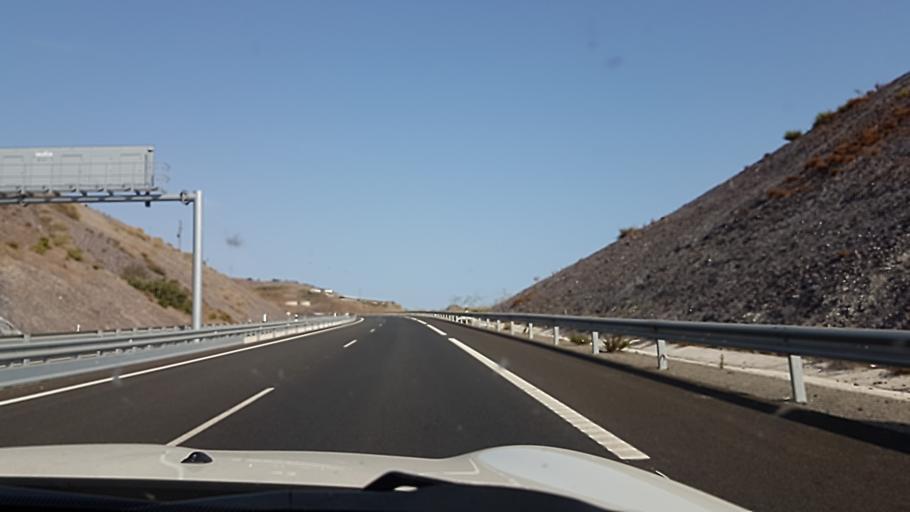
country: ES
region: Andalusia
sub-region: Provincia de Granada
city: Albunol
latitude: 36.7565
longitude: -3.2345
